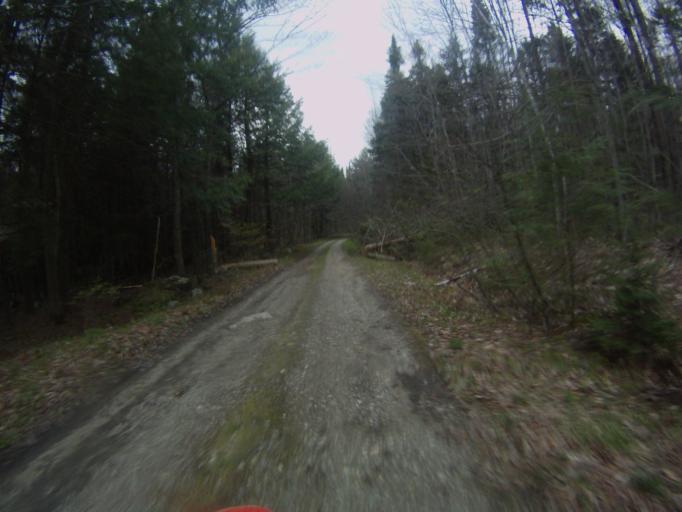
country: US
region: Vermont
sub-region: Addison County
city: Bristol
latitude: 44.0535
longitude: -73.0506
